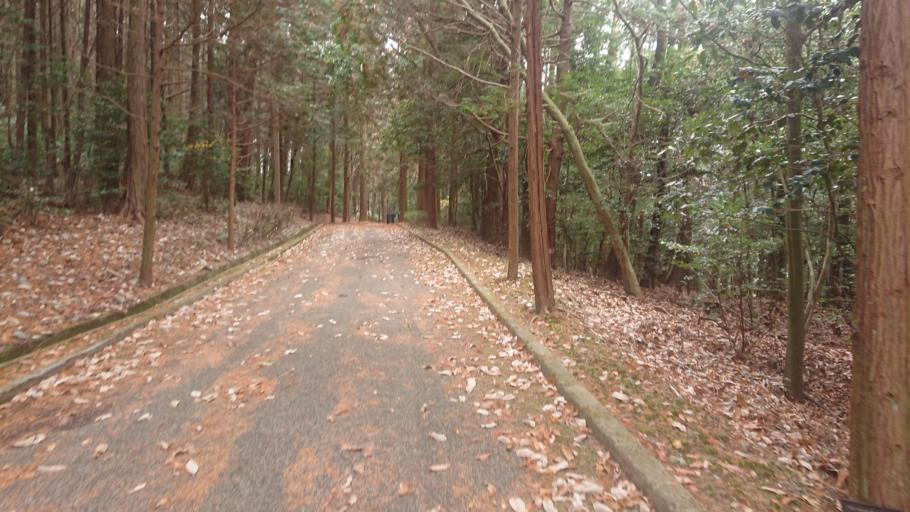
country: JP
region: Kyoto
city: Kameoka
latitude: 35.0425
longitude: 135.5870
